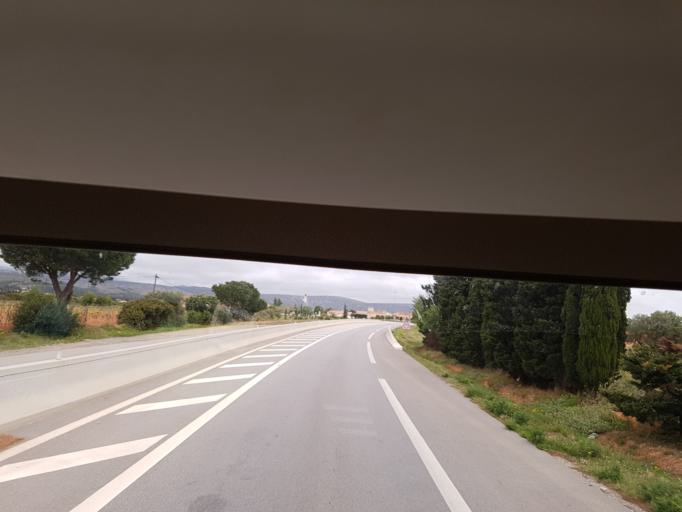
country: FR
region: Languedoc-Roussillon
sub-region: Departement des Pyrenees-Orientales
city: Salses-le-Chateau
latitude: 42.8213
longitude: 2.9163
